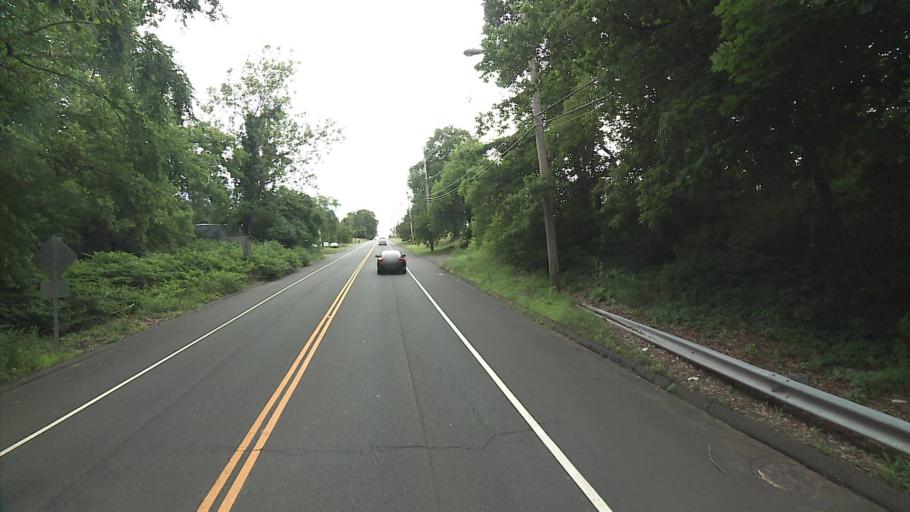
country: US
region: Connecticut
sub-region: New Haven County
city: Meriden
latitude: 41.4999
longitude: -72.8132
